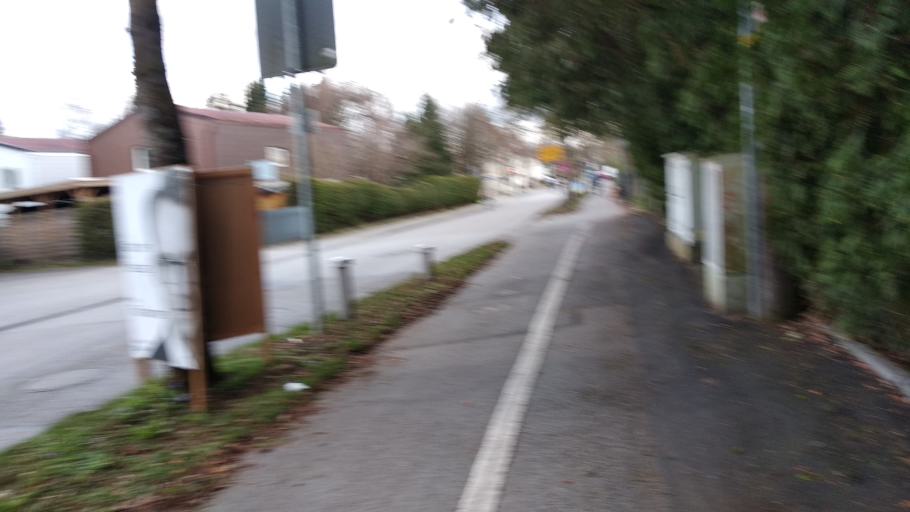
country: DE
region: Bavaria
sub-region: Upper Bavaria
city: Neubiberg
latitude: 48.0786
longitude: 11.6767
